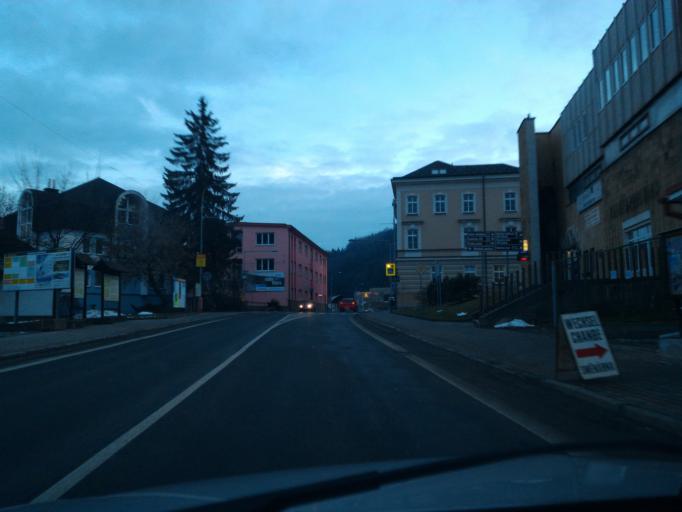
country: CZ
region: Liberecky
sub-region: Okres Jablonec nad Nisou
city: Tanvald
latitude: 50.7380
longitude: 15.3079
